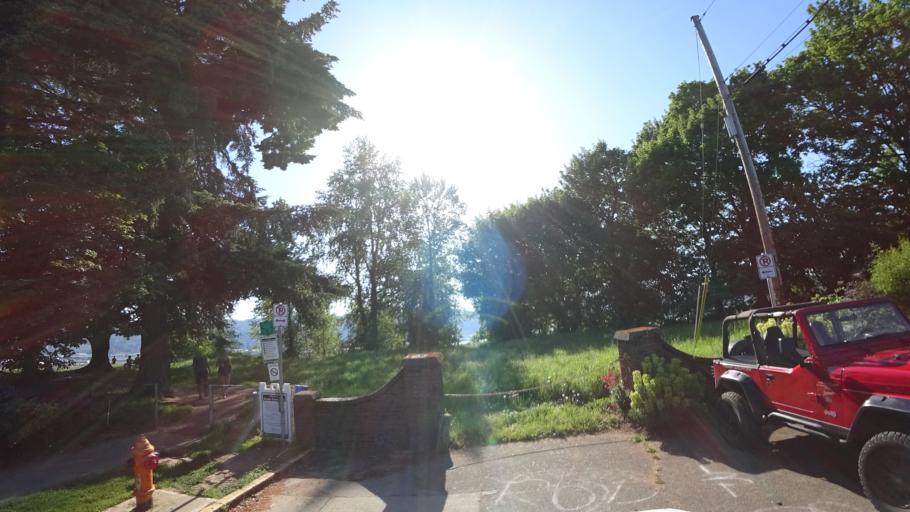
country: US
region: Oregon
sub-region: Multnomah County
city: Portland
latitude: 45.5550
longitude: -122.6910
